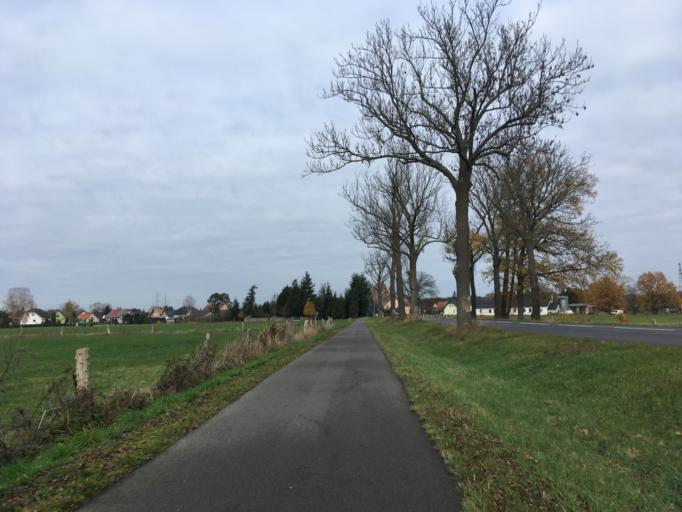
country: DE
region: Brandenburg
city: Peitz
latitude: 51.8797
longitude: 14.4191
